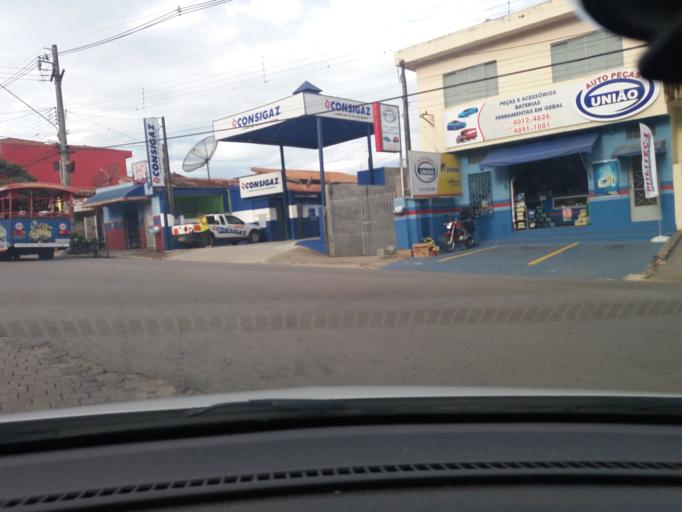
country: BR
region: Sao Paulo
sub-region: Bom Jesus Dos Perdoes
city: Bom Jesus dos Perdoes
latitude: -23.1302
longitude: -46.4668
